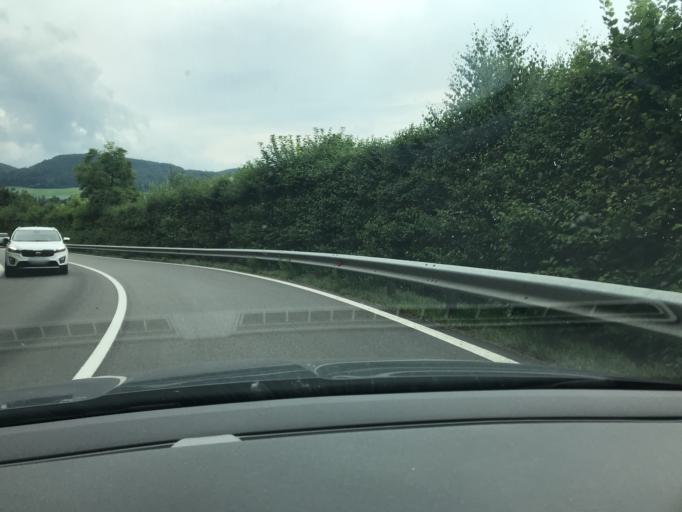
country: IT
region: Trentino-Alto Adige
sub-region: Bolzano
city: Ponte Gardena
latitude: 46.6066
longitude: 11.5416
